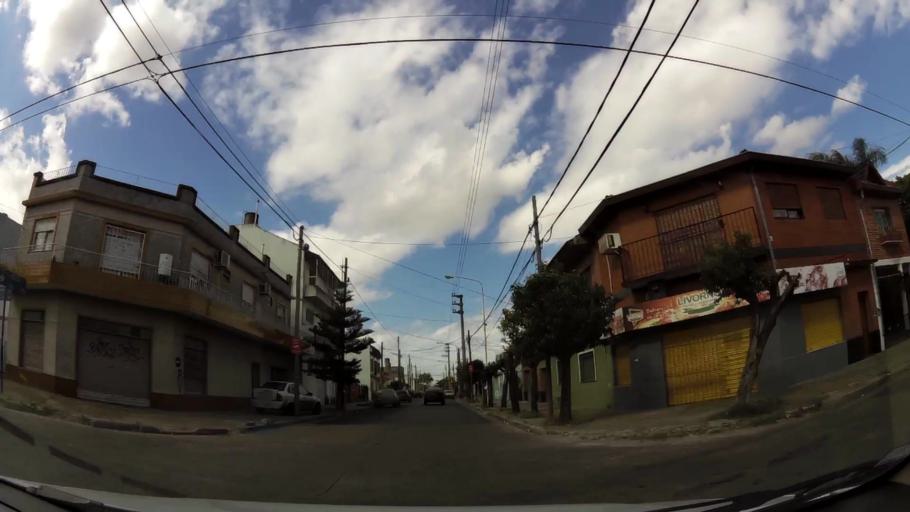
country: AR
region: Buenos Aires
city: San Justo
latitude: -34.6661
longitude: -58.5575
